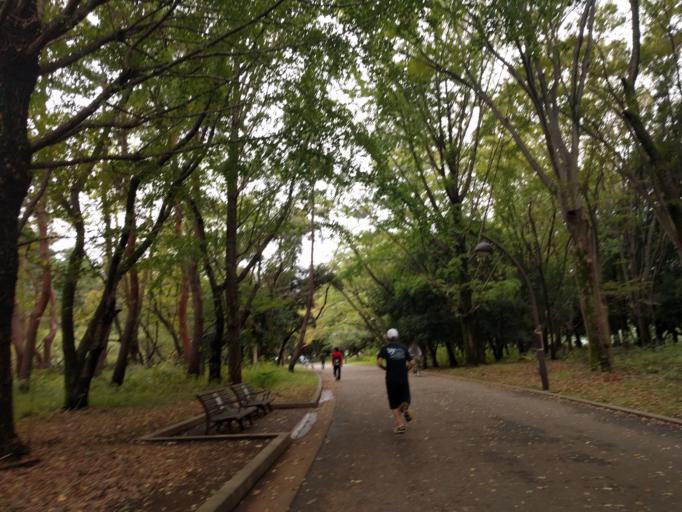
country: JP
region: Saitama
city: Wako
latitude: 35.7690
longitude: 139.6265
